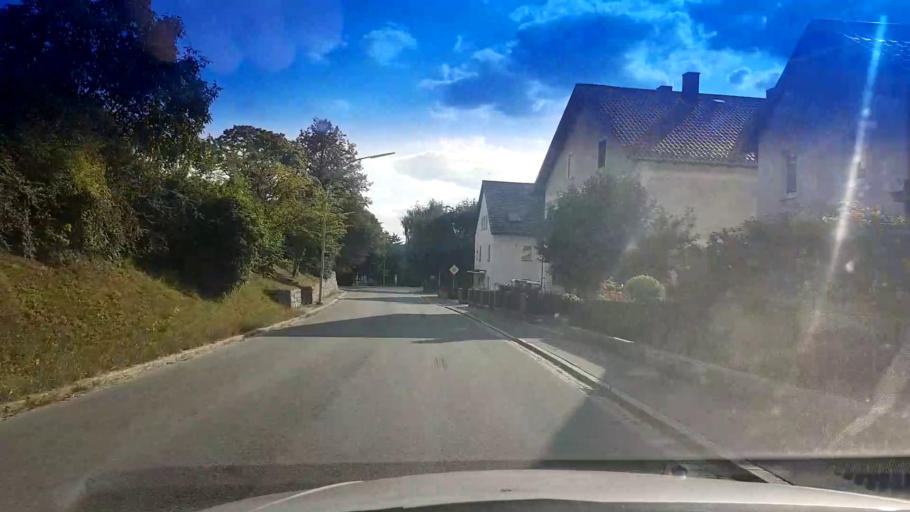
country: DE
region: Bavaria
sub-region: Upper Palatinate
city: Tirschenreuth
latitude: 49.9095
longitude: 12.3865
